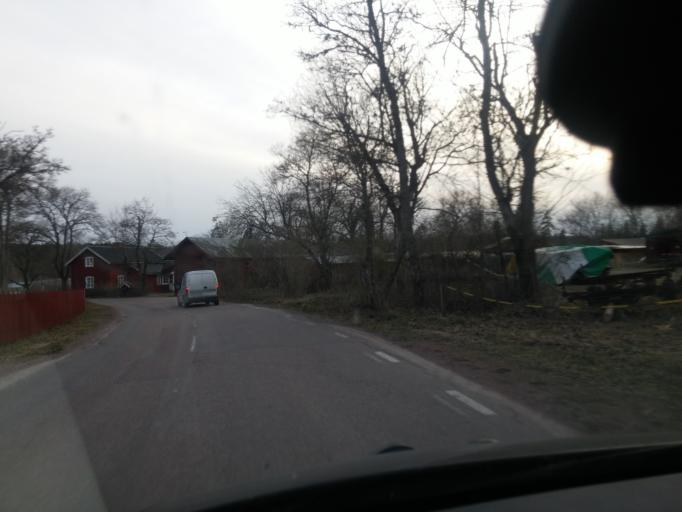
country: SE
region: Dalarna
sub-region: Borlange Kommun
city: Borlaenge
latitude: 60.5811
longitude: 15.4088
